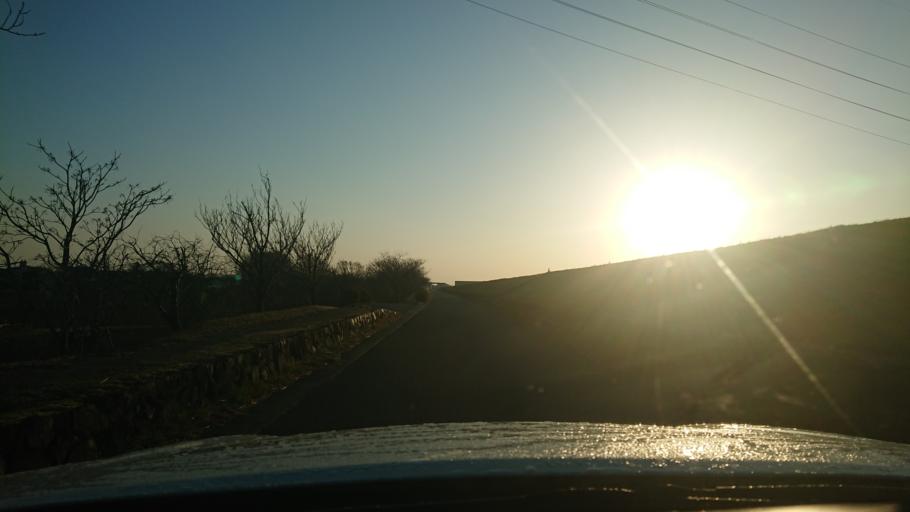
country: JP
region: Tokushima
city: Anan
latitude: 33.9409
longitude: 134.6039
